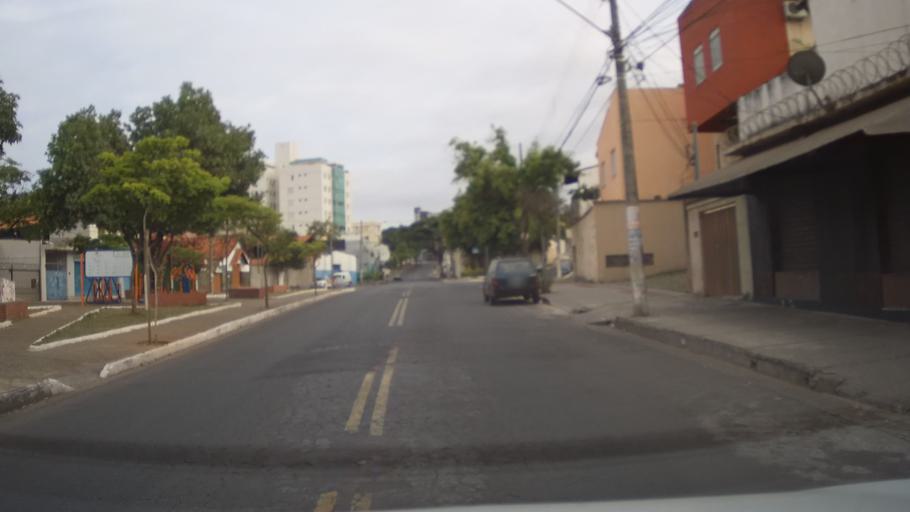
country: BR
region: Minas Gerais
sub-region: Belo Horizonte
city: Belo Horizonte
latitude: -19.9090
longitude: -43.9750
